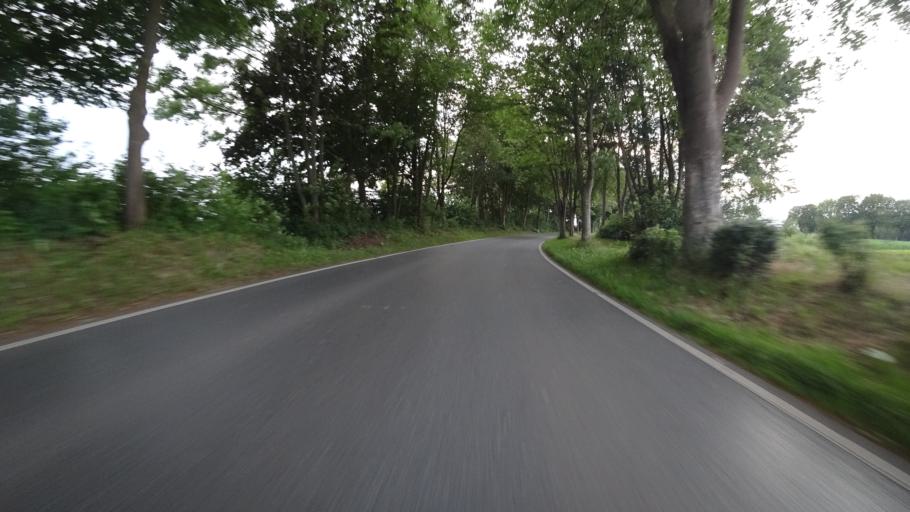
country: DE
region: North Rhine-Westphalia
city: Erwitte
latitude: 51.6276
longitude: 8.3523
